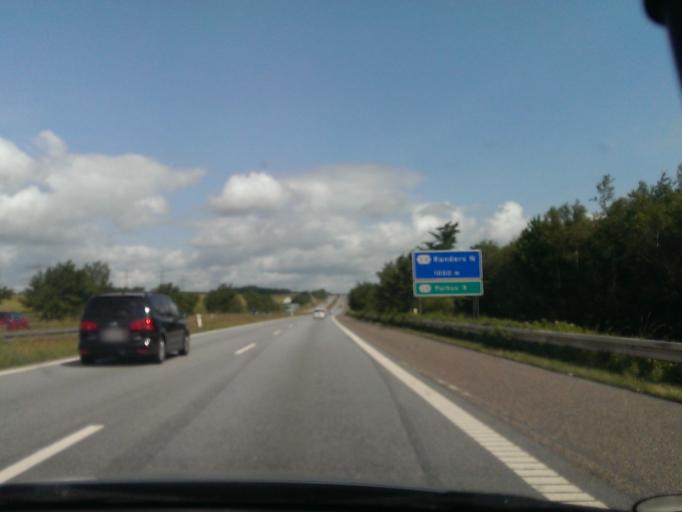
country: DK
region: Central Jutland
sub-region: Randers Kommune
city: Randers
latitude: 56.4767
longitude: 9.9819
